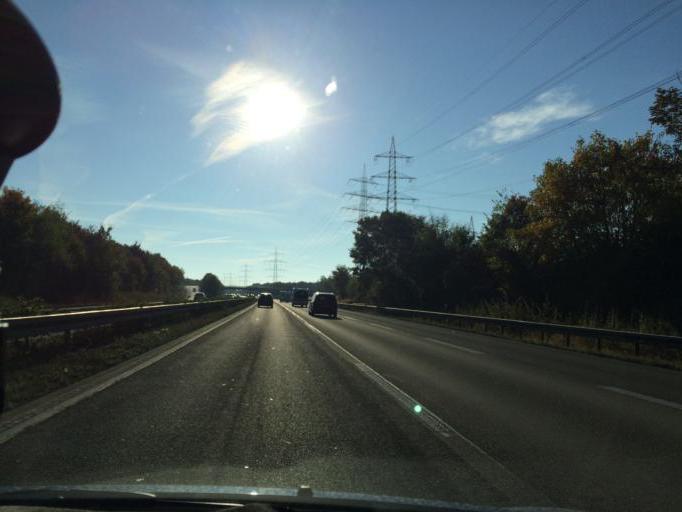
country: DE
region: North Rhine-Westphalia
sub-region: Regierungsbezirk Koln
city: Wahn-Heide
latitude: 50.8209
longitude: 7.1061
